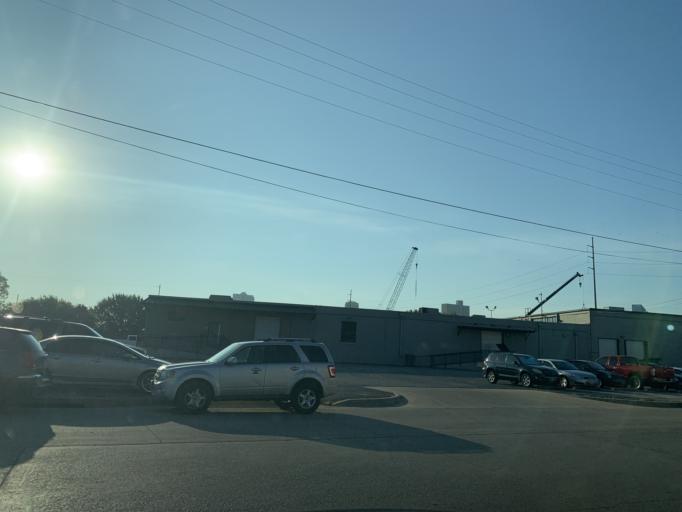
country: US
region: Texas
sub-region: Tarrant County
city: Fort Worth
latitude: 32.7602
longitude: -97.3495
